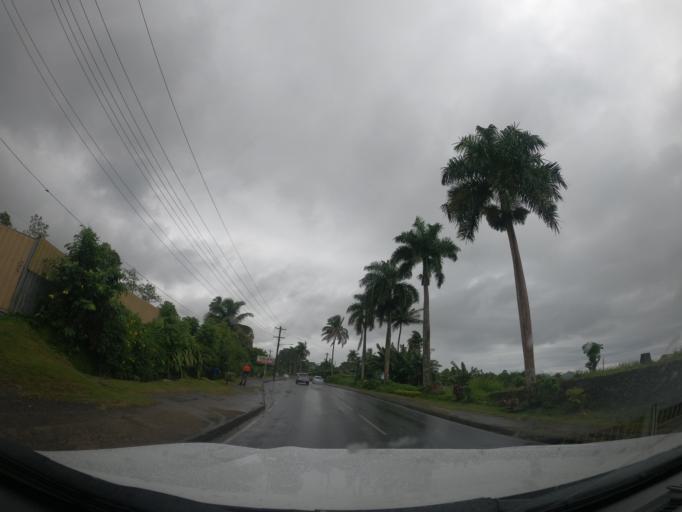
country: FJ
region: Central
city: Suva
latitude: -18.1133
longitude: 178.4203
